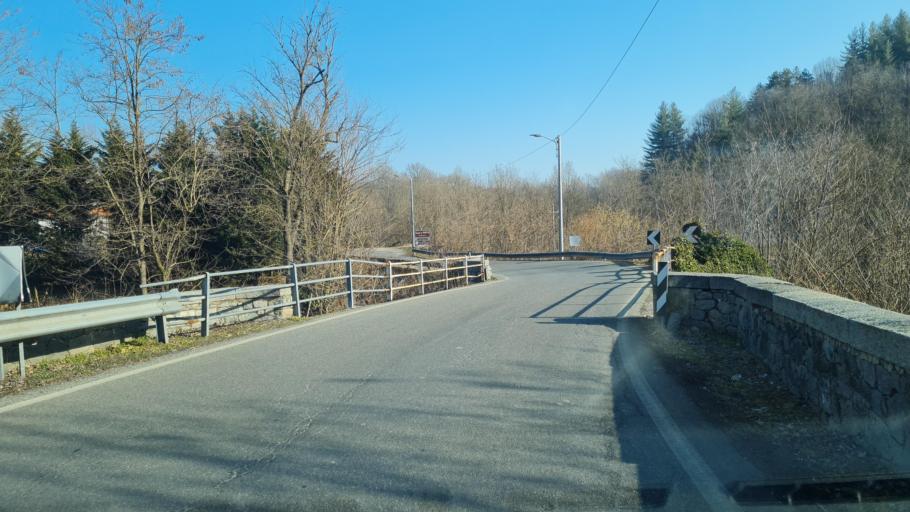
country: IT
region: Piedmont
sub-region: Provincia di Biella
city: Piatto
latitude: 45.5789
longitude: 8.1379
